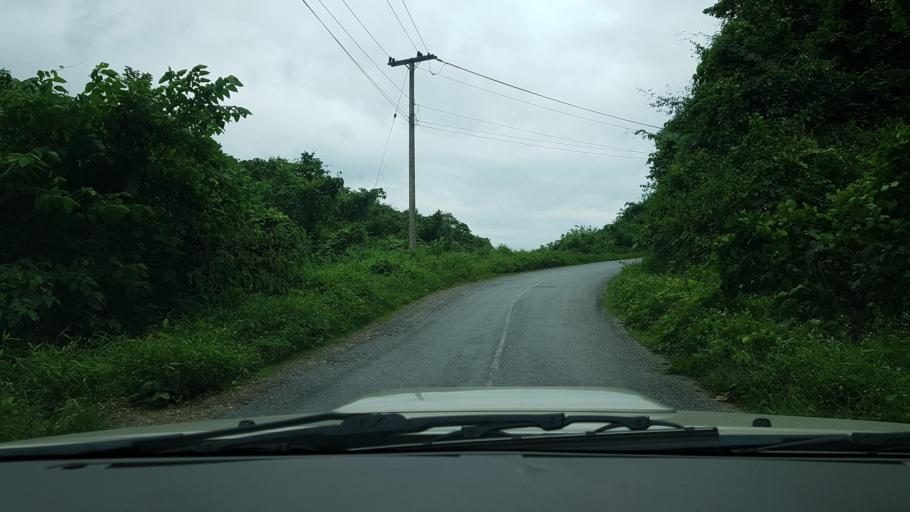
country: LA
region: Oudomxai
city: Muang La
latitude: 21.0061
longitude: 102.2342
